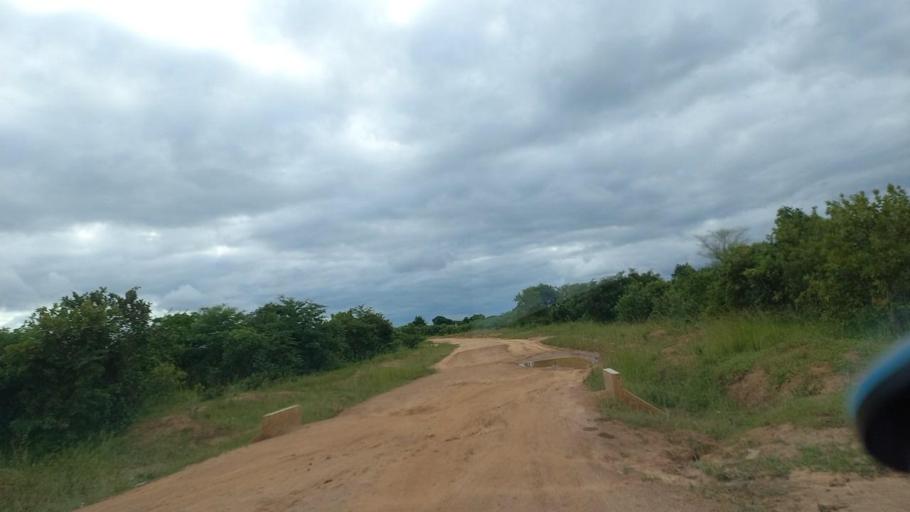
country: ZM
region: Lusaka
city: Chongwe
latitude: -15.4496
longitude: 28.8424
